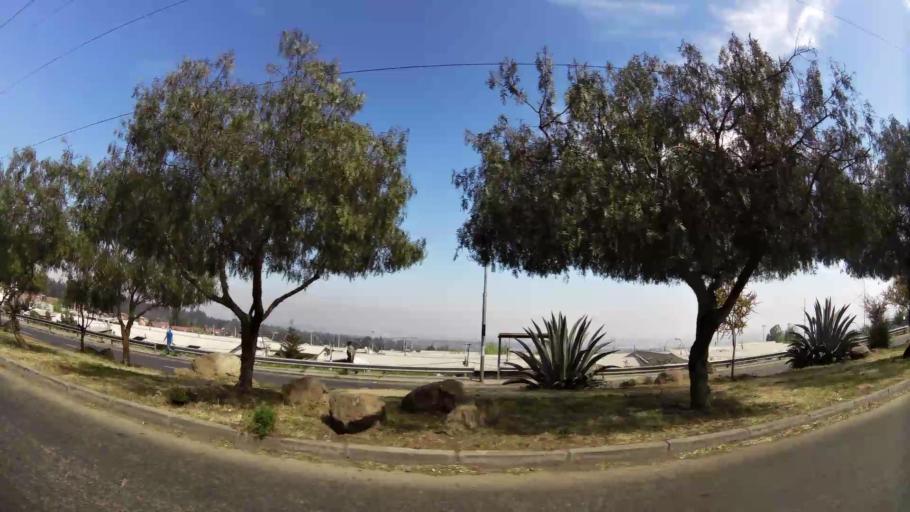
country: CL
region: Santiago Metropolitan
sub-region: Provincia de Santiago
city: Villa Presidente Frei, Nunoa, Santiago, Chile
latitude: -33.4802
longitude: -70.5240
